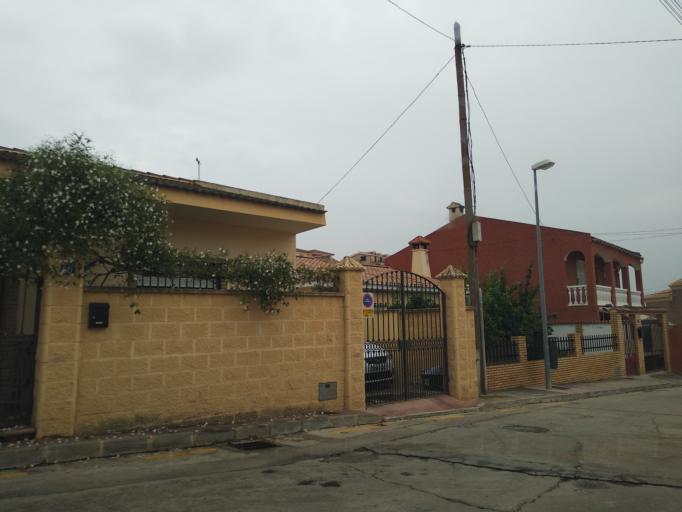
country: ES
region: Andalusia
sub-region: Provincia de Malaga
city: Malaga
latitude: 36.7459
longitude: -4.4775
